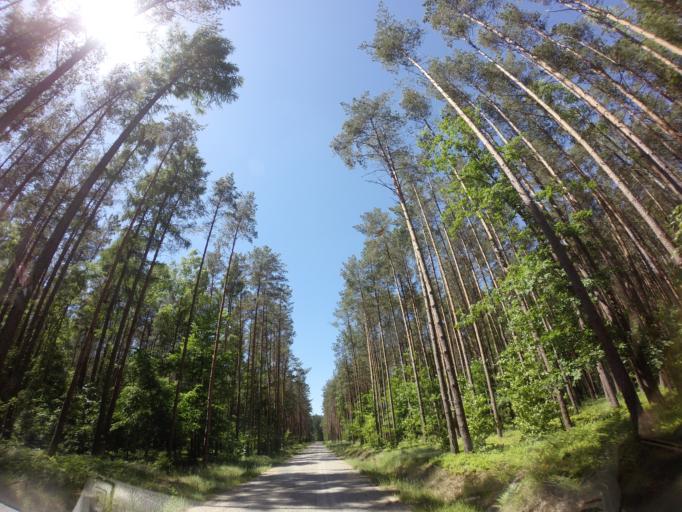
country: PL
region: Lubusz
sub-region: Powiat strzelecko-drezdenecki
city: Dobiegniew
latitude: 53.0746
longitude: 15.8389
